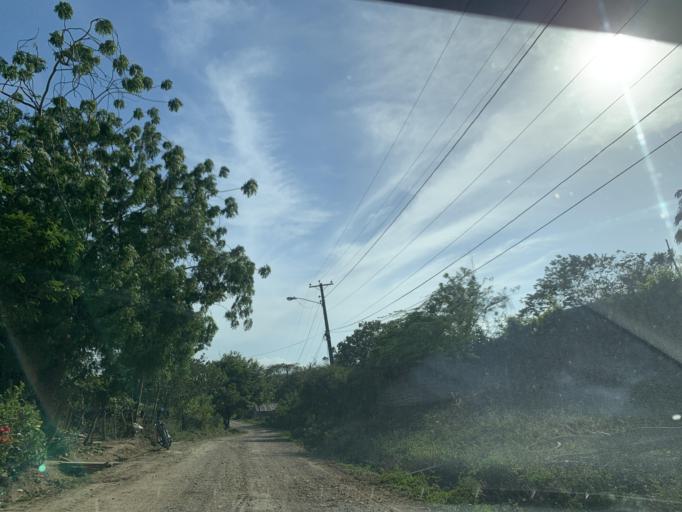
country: DO
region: Puerto Plata
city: Luperon
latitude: 19.8834
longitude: -70.9228
